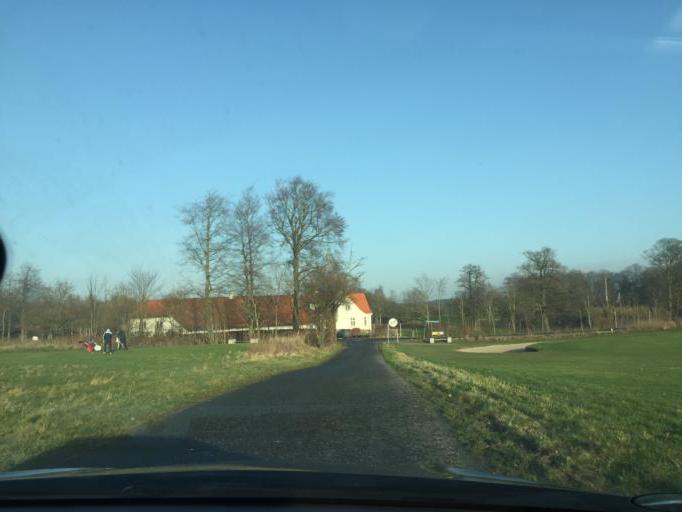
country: DK
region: South Denmark
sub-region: Faaborg-Midtfyn Kommune
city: Faaborg
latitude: 55.1364
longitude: 10.2498
